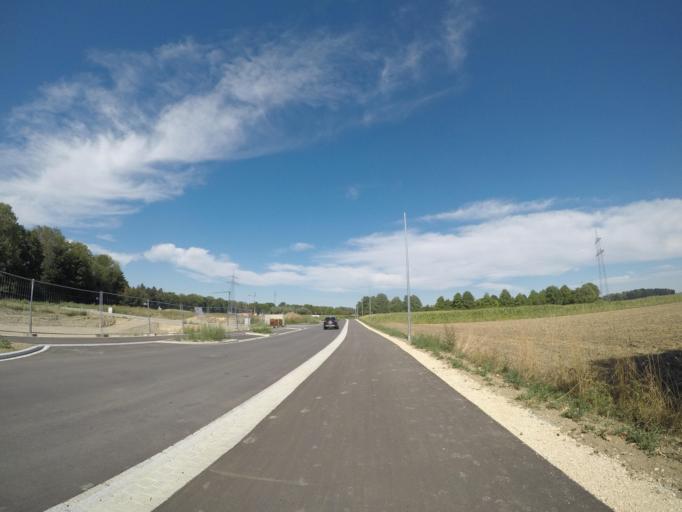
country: DE
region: Bavaria
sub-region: Swabia
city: Senden
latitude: 48.3312
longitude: 10.0277
